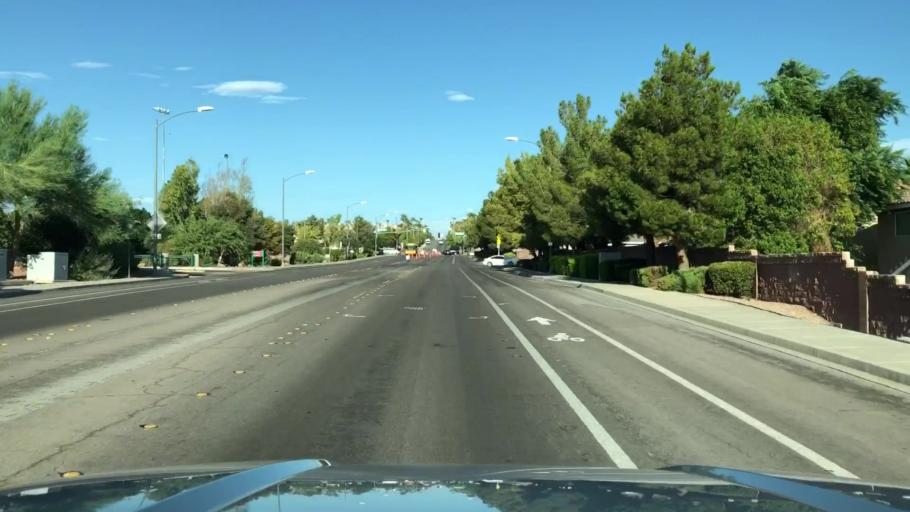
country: US
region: Nevada
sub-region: Clark County
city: Whitney
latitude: 36.0490
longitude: -115.0526
